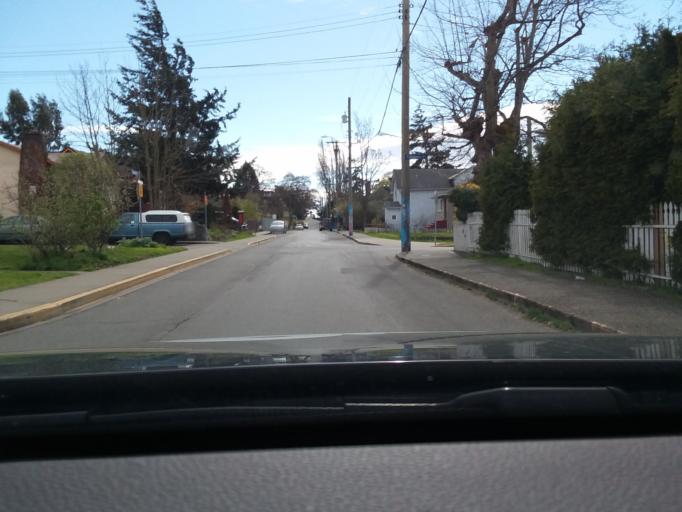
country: CA
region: British Columbia
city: Victoria
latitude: 48.4306
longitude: -123.3499
